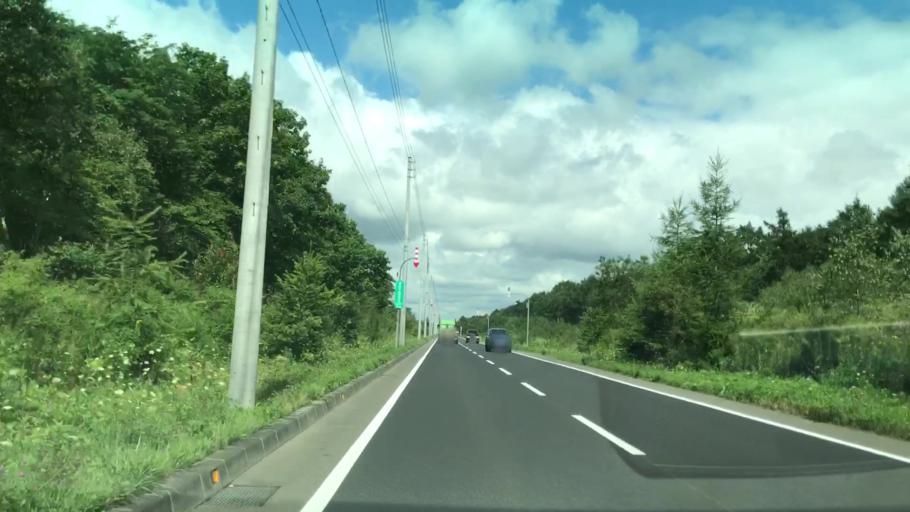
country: JP
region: Hokkaido
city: Chitose
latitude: 42.7664
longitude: 141.6632
